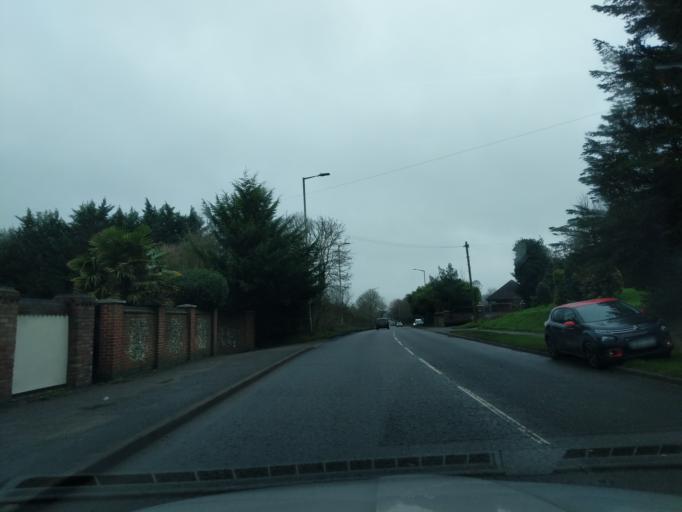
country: GB
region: England
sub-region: Hertfordshire
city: Kings Langley
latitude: 51.7246
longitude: -0.4525
